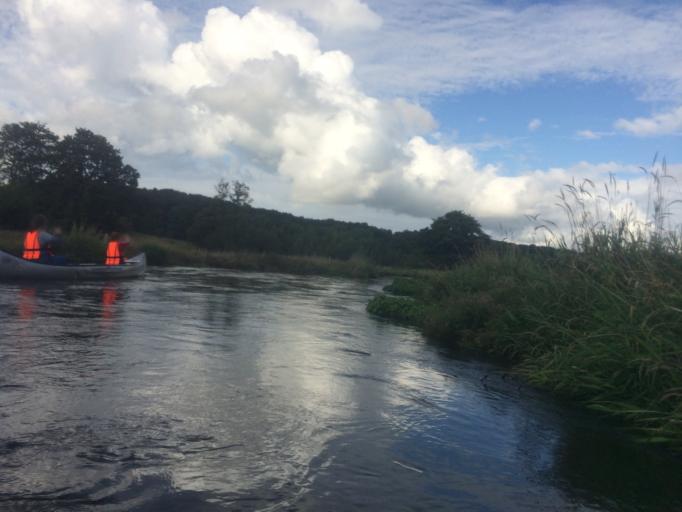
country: DK
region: South Denmark
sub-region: Vejle Kommune
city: Egtved
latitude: 55.6604
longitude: 9.3160
